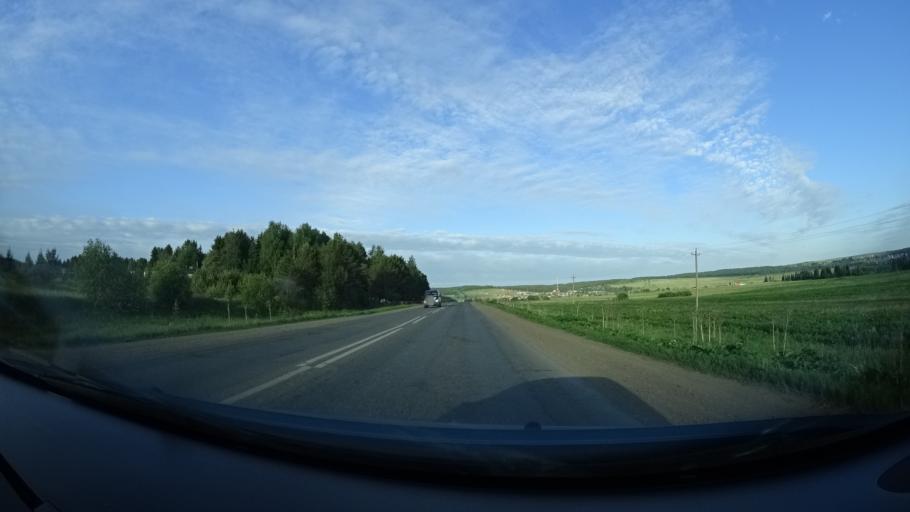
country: RU
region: Perm
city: Kultayevo
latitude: 57.8601
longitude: 55.8697
